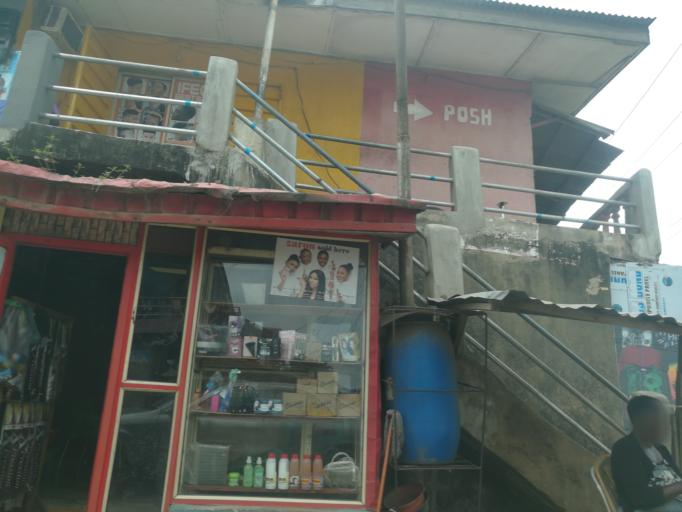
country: NG
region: Lagos
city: Ikorodu
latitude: 6.6123
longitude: 3.5118
